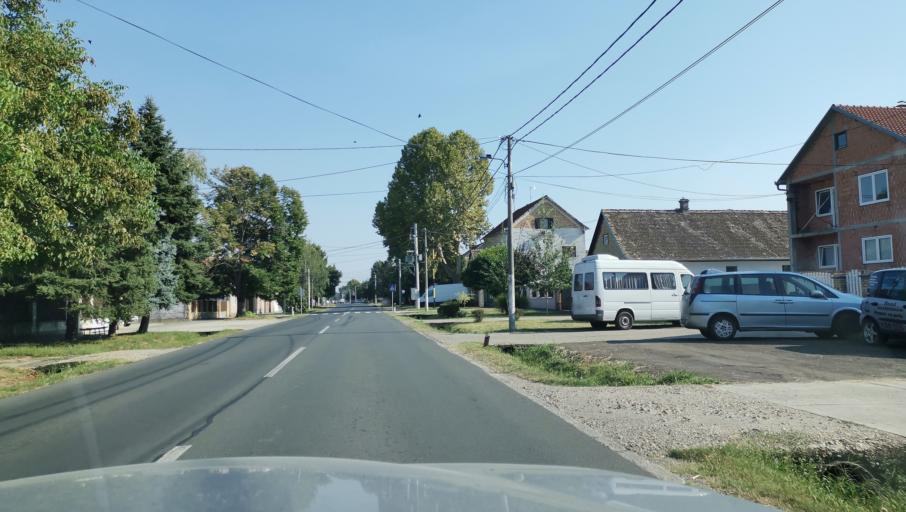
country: RS
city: Dobanovci
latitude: 44.8358
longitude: 20.2166
